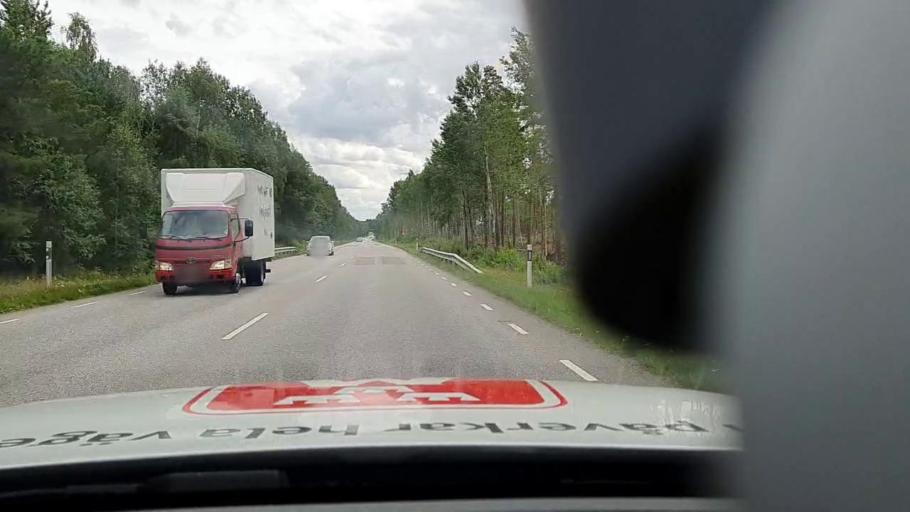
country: SE
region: Vaestra Goetaland
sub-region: Lidkopings Kommun
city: Lidkoping
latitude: 58.5294
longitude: 13.1108
